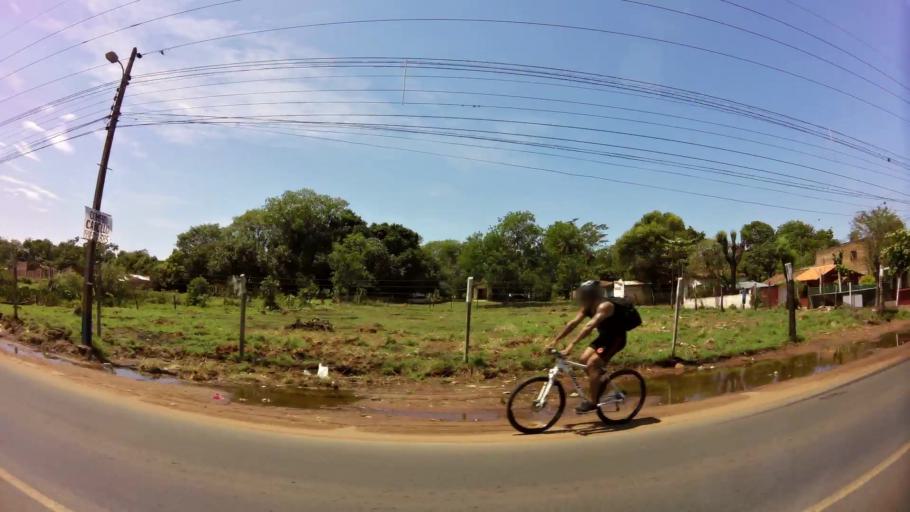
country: PY
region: Central
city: Nemby
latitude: -25.3946
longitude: -57.5285
